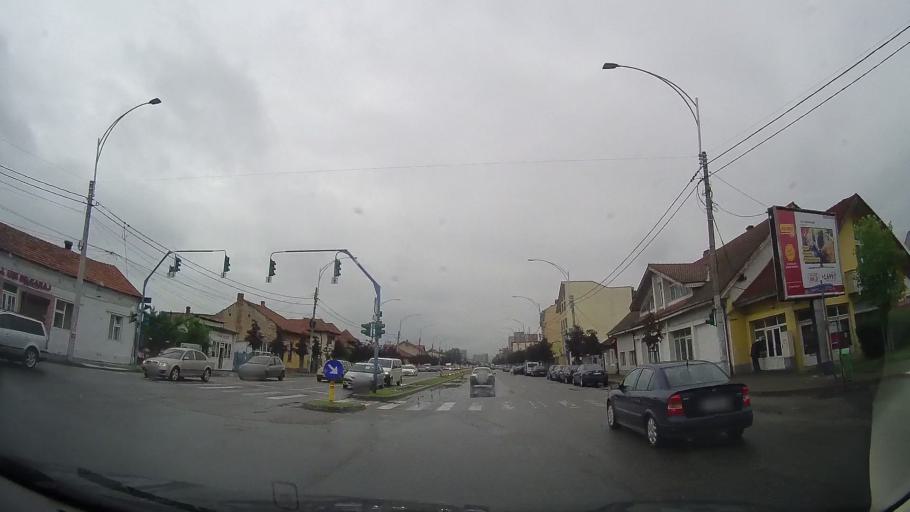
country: RO
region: Mehedinti
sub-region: Municipiul Drobeta-Turnu Severin
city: Drobeta-Turnu Severin
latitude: 44.6312
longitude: 22.6469
